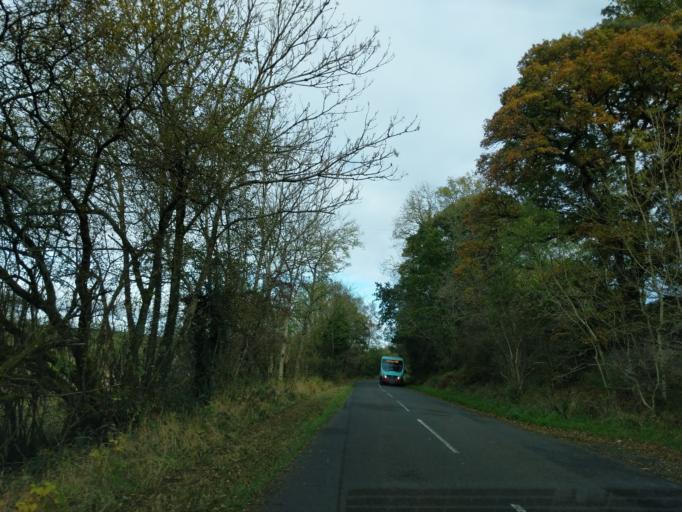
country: GB
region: Scotland
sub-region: Dumfries and Galloway
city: Castle Douglas
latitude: 55.0994
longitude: -4.1233
